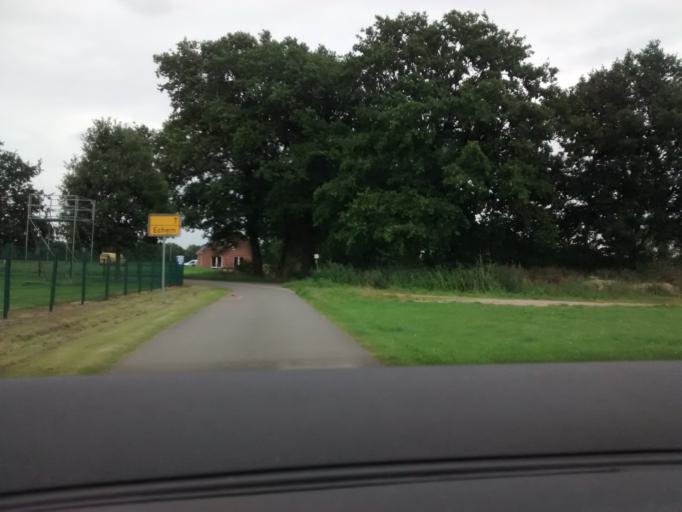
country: DE
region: Lower Saxony
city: Echem
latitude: 53.3368
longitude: 10.5480
